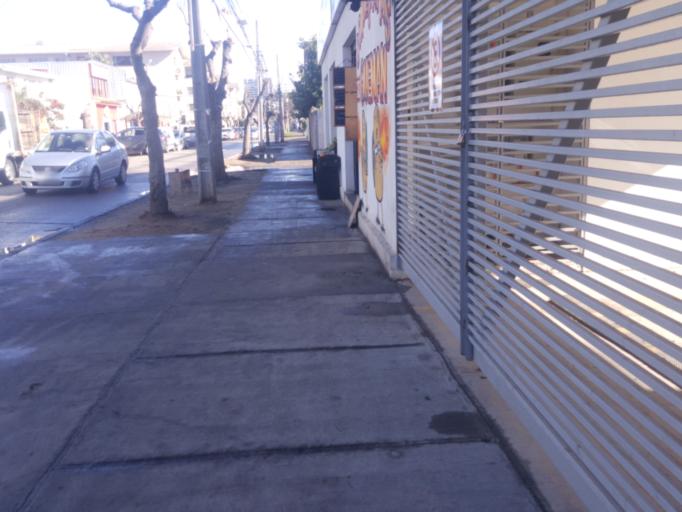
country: CL
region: Valparaiso
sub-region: Provincia de Valparaiso
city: Vina del Mar
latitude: -33.0121
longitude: -71.5433
